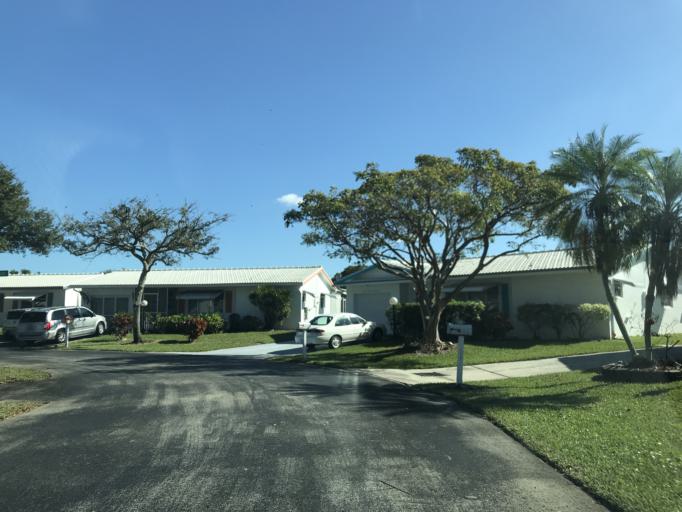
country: US
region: Florida
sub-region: Broward County
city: Plantation
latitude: 26.1360
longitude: -80.2689
